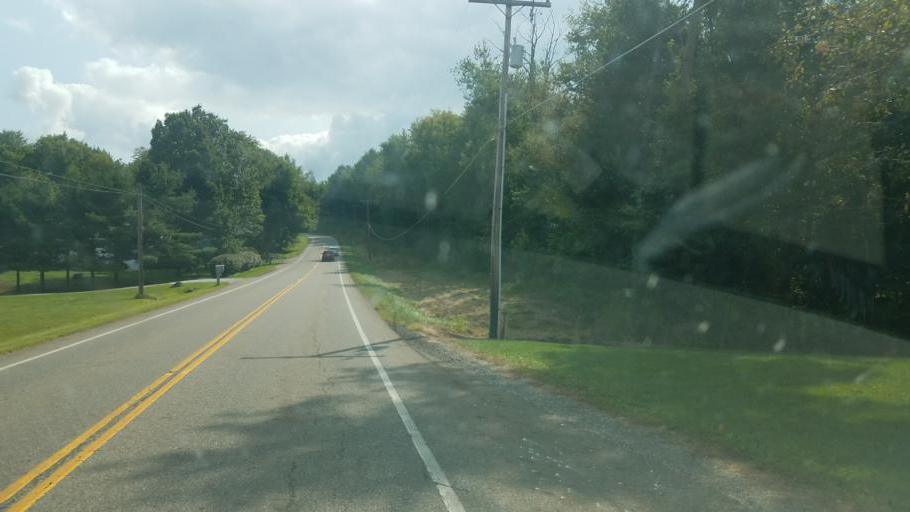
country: US
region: Ohio
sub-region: Stark County
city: East Canton
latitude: 40.7950
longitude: -81.2501
